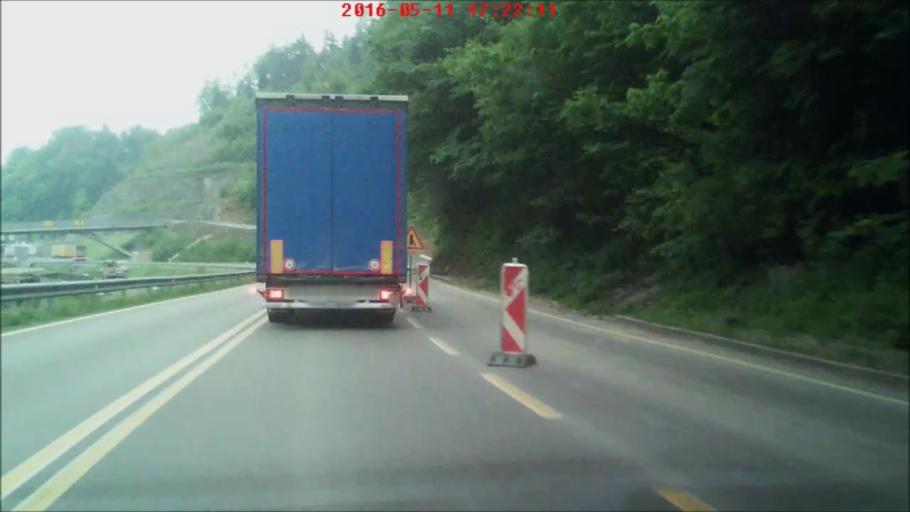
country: SI
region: Zetale
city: Zetale
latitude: 46.2807
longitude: 15.8616
